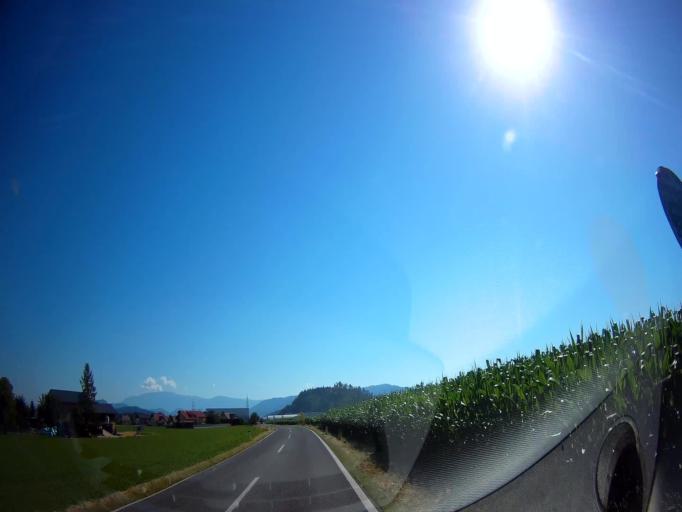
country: AT
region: Carinthia
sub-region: Politischer Bezirk Volkermarkt
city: Globasnitz
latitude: 46.5747
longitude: 14.7227
